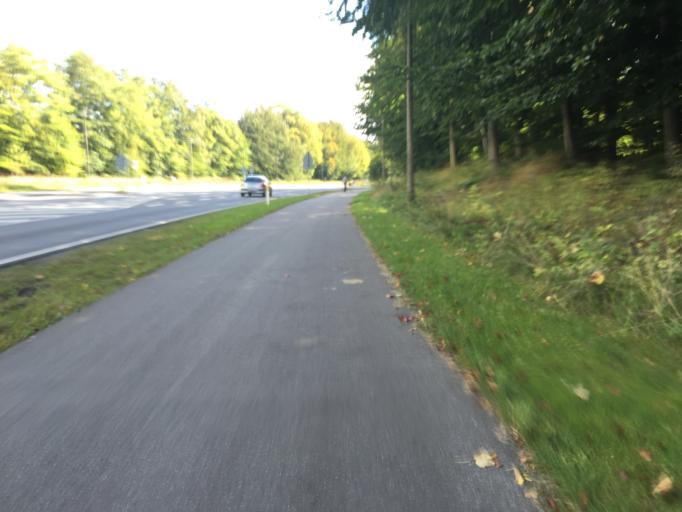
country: DK
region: Capital Region
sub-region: Fureso Kommune
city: Stavnsholt
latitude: 55.7712
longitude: 12.4267
